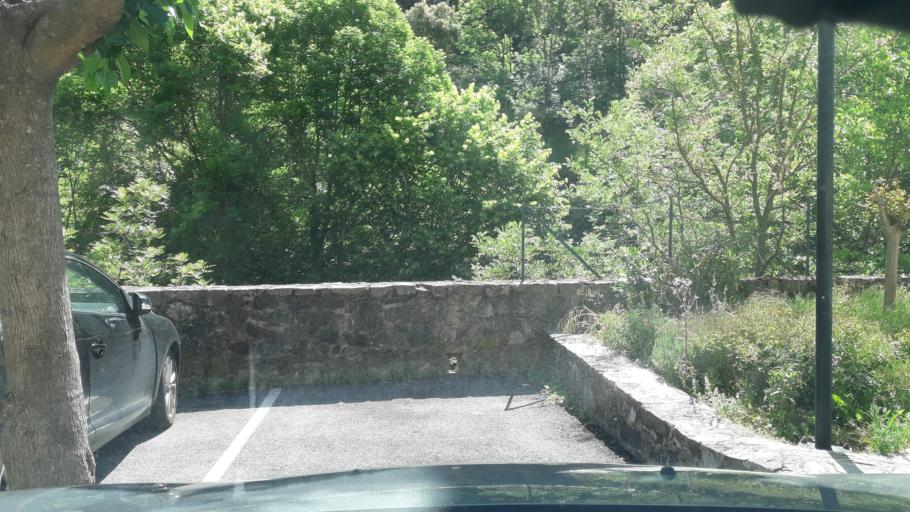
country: FR
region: Languedoc-Roussillon
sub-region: Departement du Gard
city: Valleraugue
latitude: 44.1162
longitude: 3.7231
